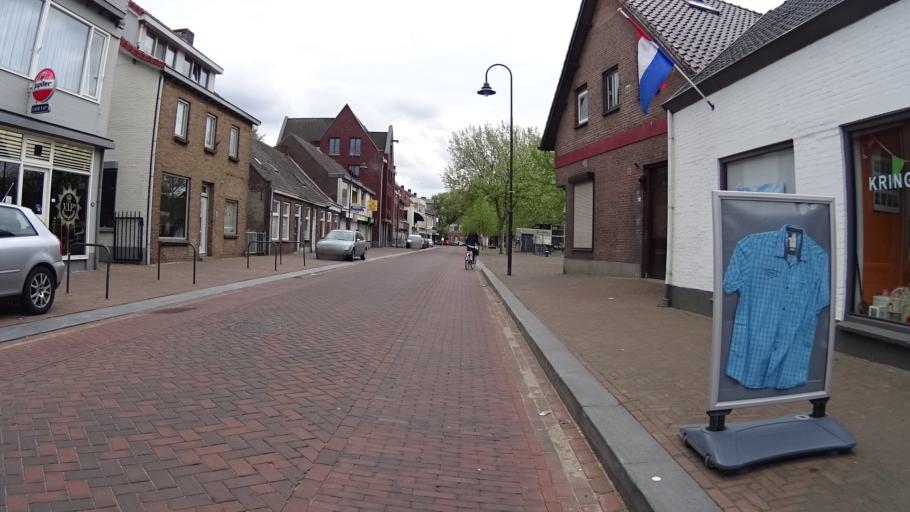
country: NL
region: North Brabant
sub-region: Gemeente Veghel
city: Veghel
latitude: 51.6159
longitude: 5.5354
